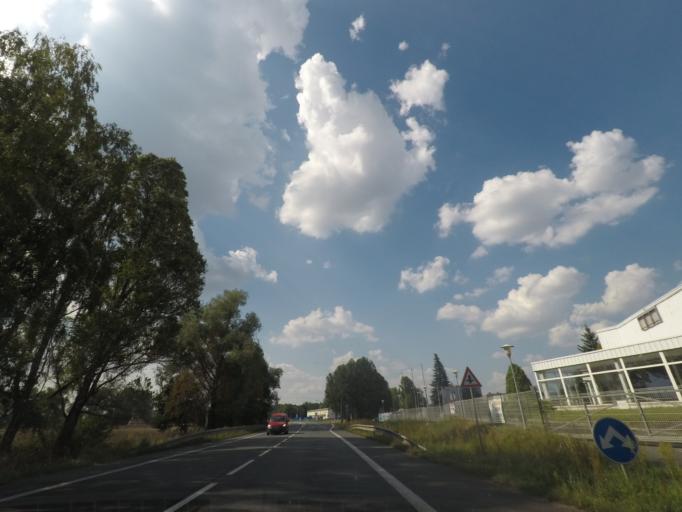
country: CZ
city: Tyniste nad Orlici
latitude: 50.1560
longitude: 16.0655
